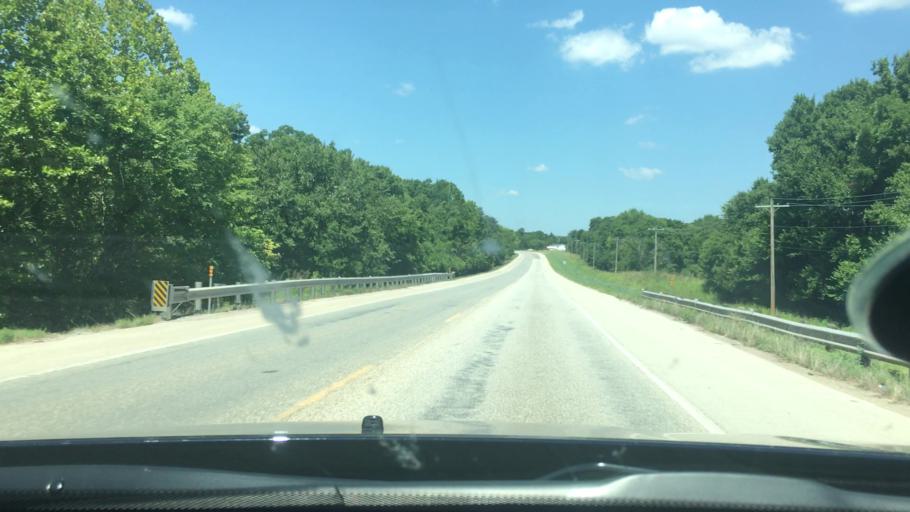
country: US
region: Oklahoma
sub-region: Marshall County
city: Oakland
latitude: 34.1819
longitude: -96.8677
